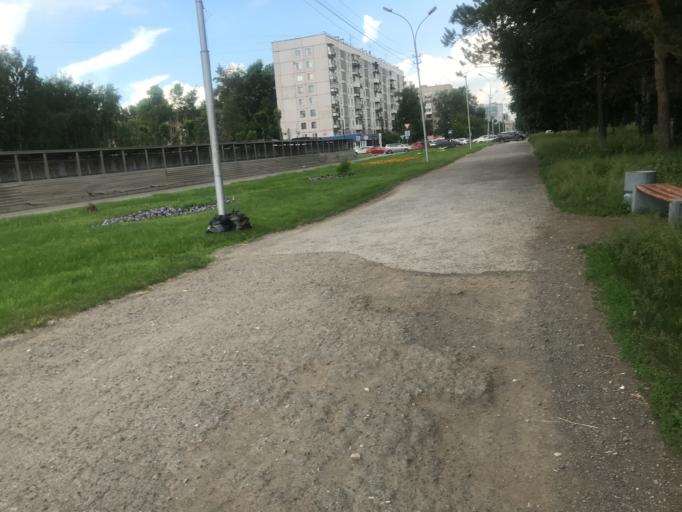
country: RU
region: Novosibirsk
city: Krasnoobsk
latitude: 54.9405
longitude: 82.9111
